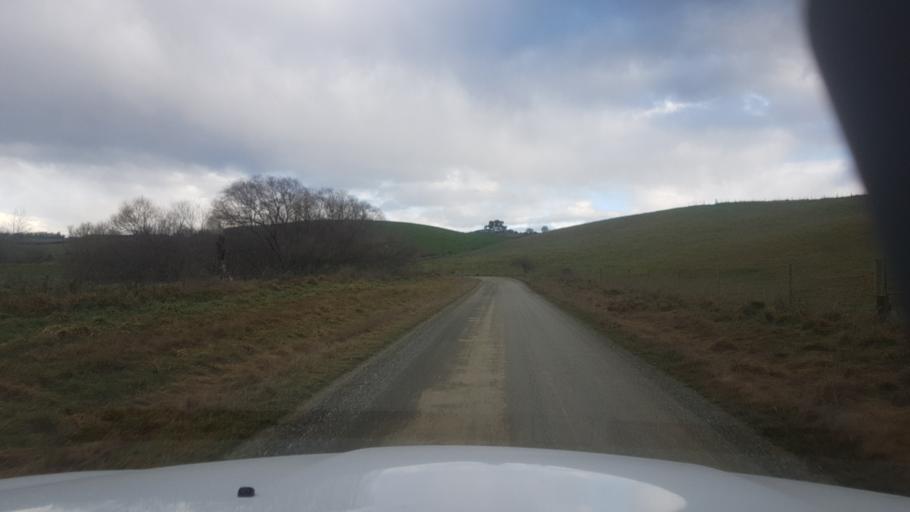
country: NZ
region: Canterbury
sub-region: Timaru District
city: Pleasant Point
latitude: -44.3404
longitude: 171.1679
